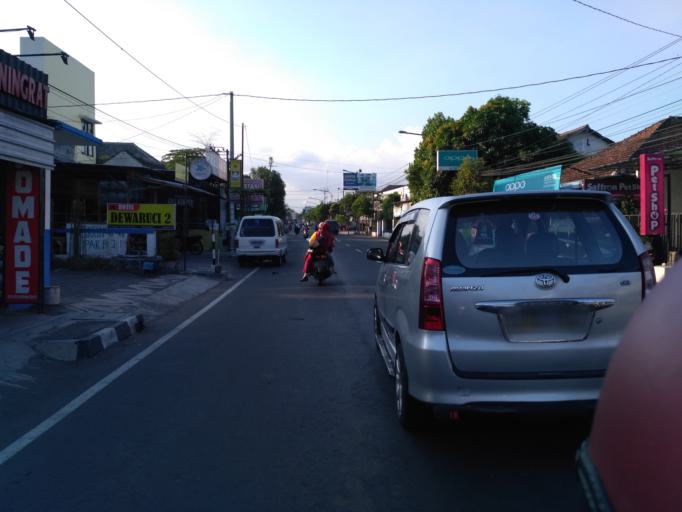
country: ID
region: Daerah Istimewa Yogyakarta
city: Yogyakarta
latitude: -7.8287
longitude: 110.3899
